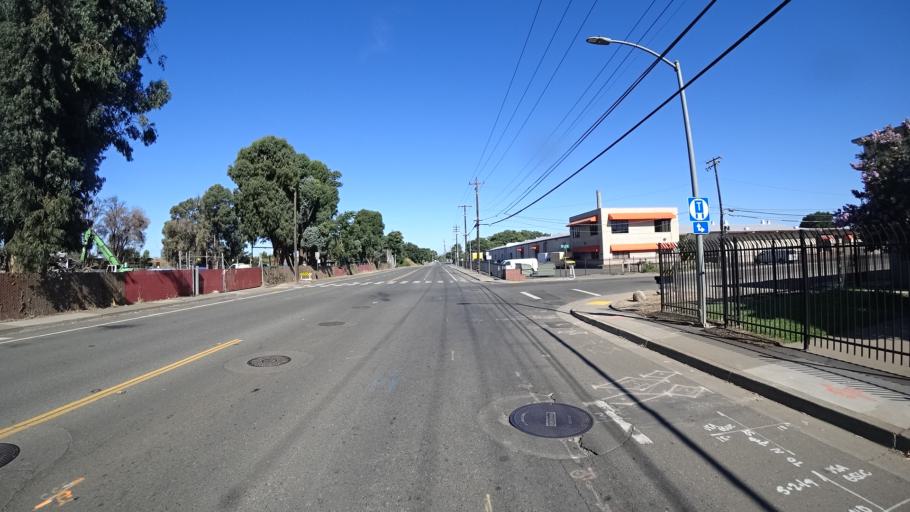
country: US
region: California
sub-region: Sacramento County
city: Sacramento
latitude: 38.5912
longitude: -121.4884
